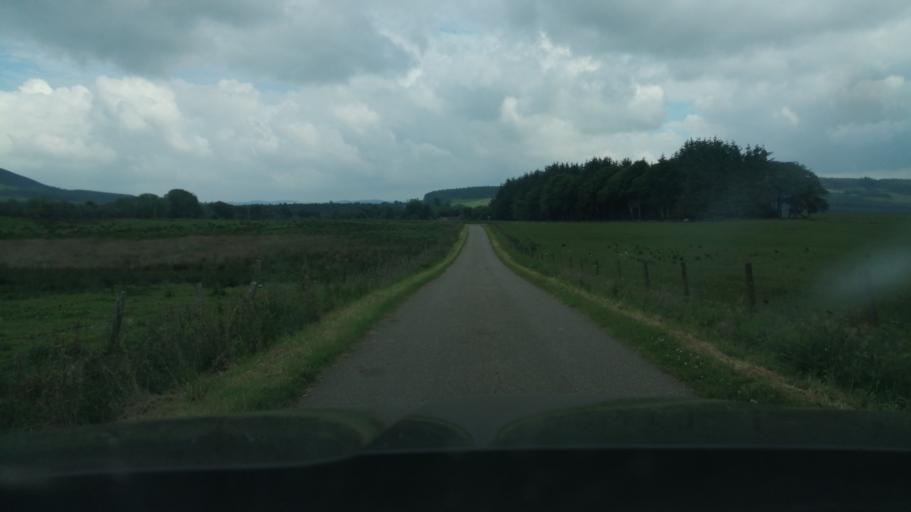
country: GB
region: Scotland
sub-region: Moray
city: Cullen
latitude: 57.5908
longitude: -2.8214
